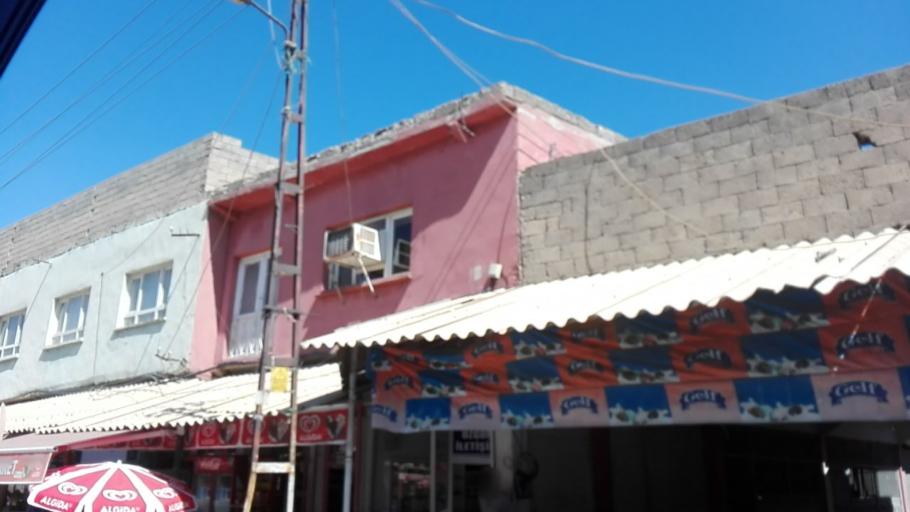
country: TR
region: Batman
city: Hasankeyf
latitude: 37.7144
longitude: 41.4133
